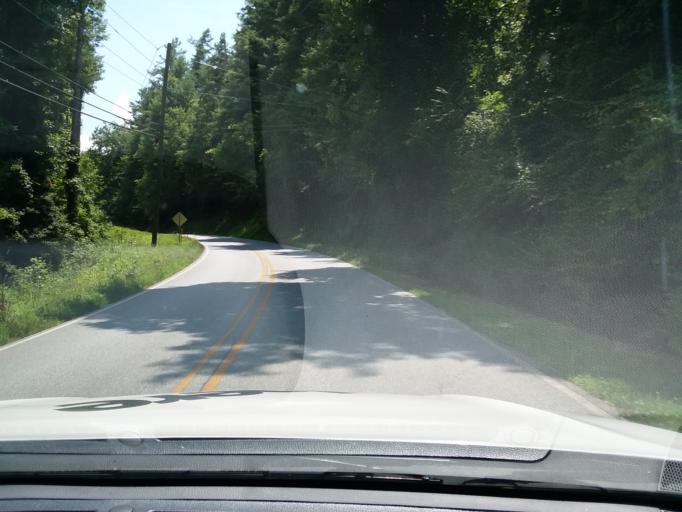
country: US
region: Georgia
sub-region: Rabun County
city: Clayton
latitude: 34.7887
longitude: -83.4173
